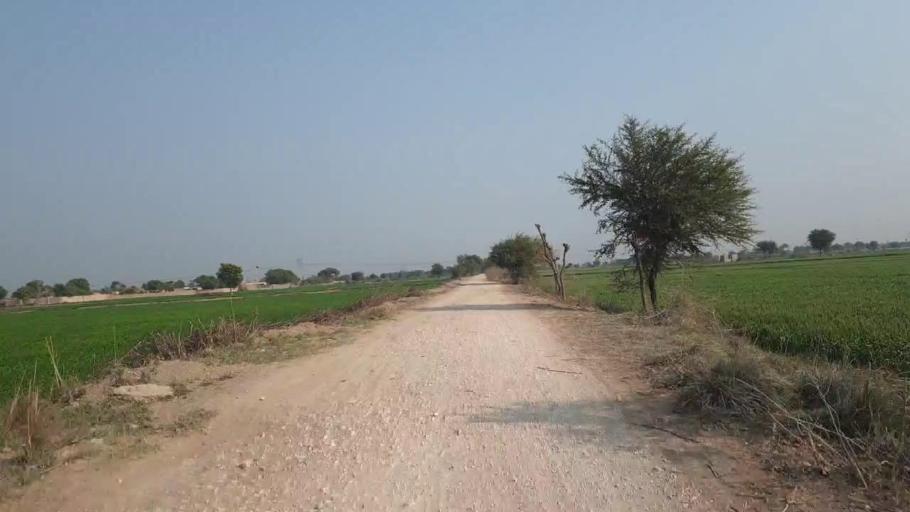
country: PK
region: Sindh
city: Hala
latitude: 25.8828
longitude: 68.4558
